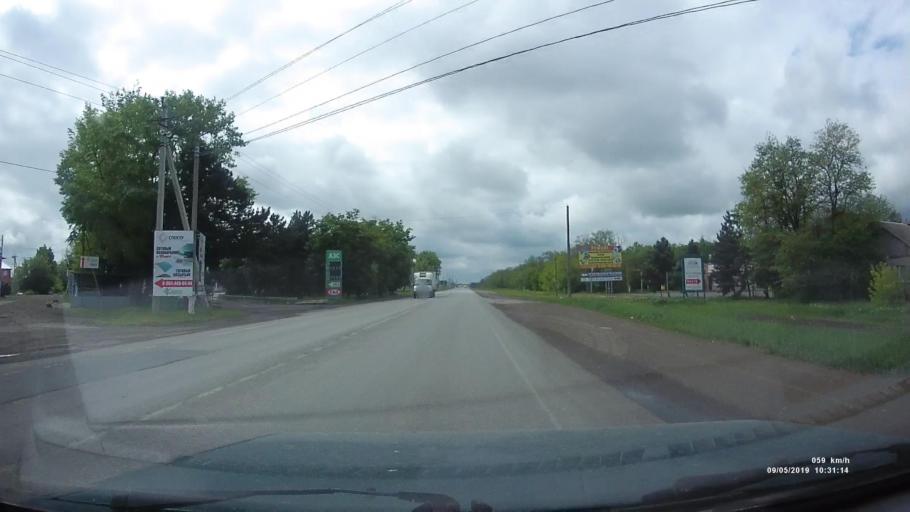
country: RU
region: Rostov
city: Azov
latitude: 47.0835
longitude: 39.4281
